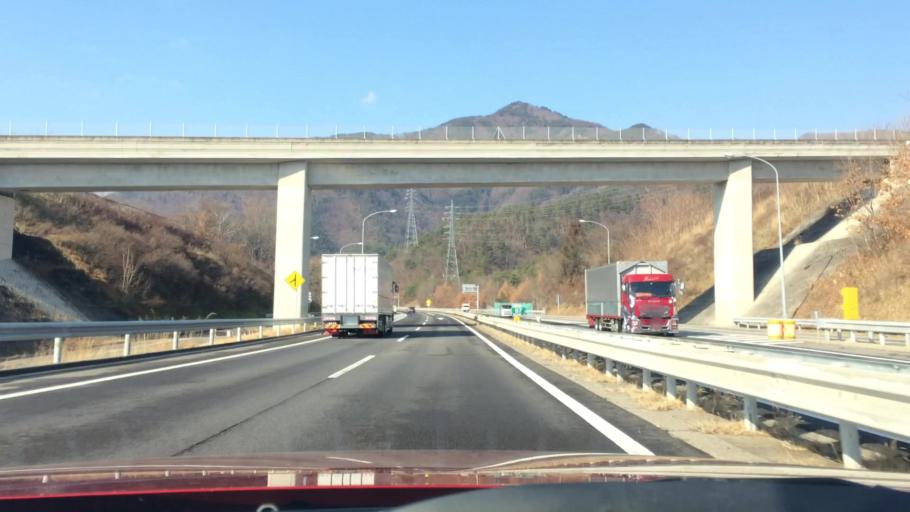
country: JP
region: Nagano
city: Ueda
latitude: 36.4150
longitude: 138.2826
